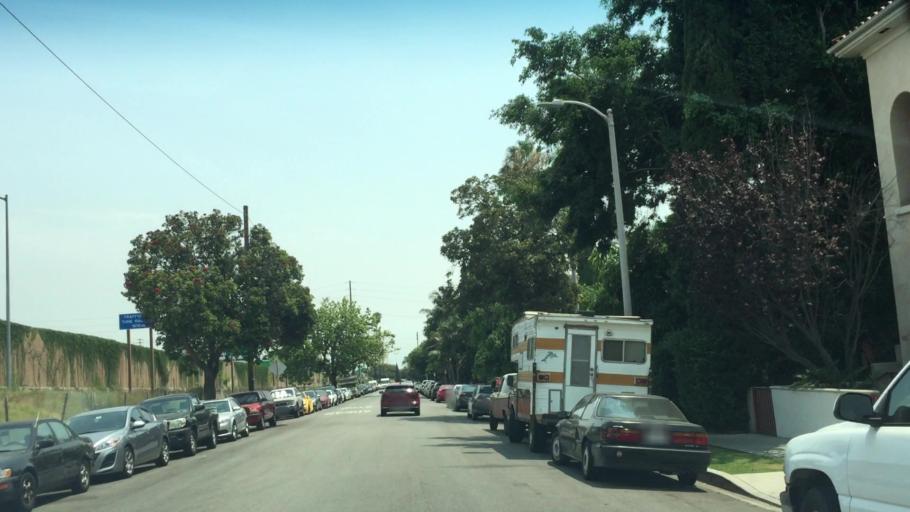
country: US
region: California
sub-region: Los Angeles County
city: Westwood, Los Angeles
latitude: 34.0443
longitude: -118.4452
